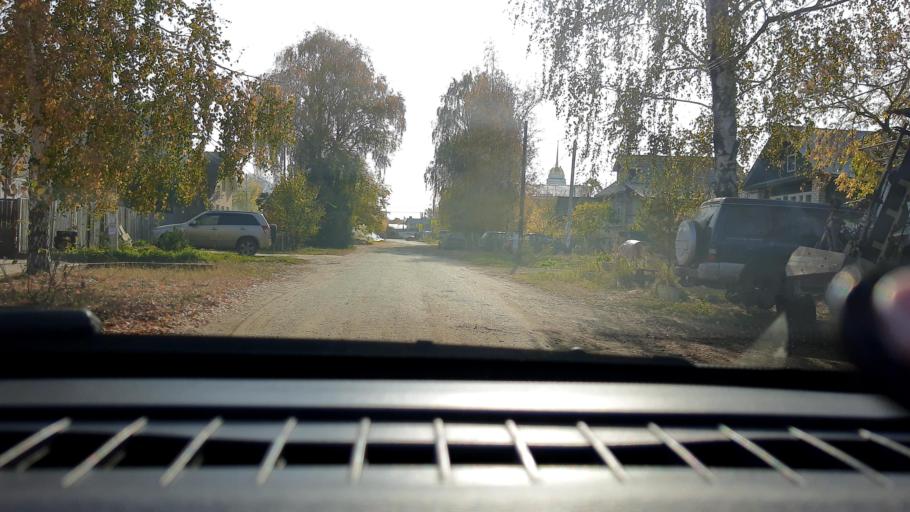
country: RU
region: Nizjnij Novgorod
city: Gorbatovka
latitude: 56.2114
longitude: 43.7552
